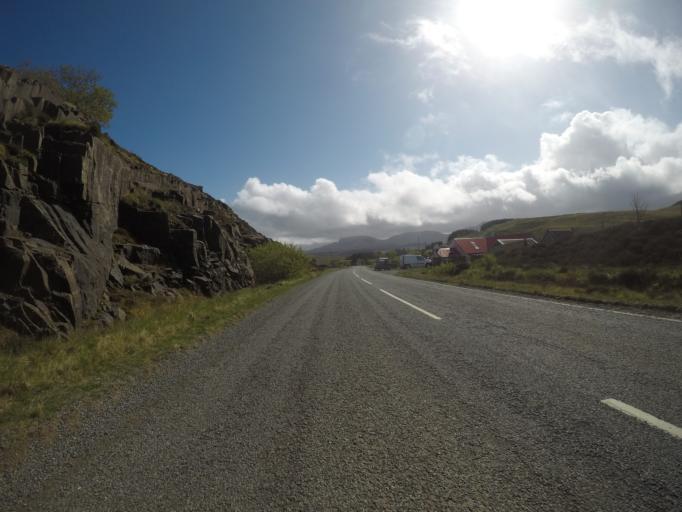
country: GB
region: Scotland
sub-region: Highland
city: Portree
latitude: 57.5861
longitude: -6.1571
